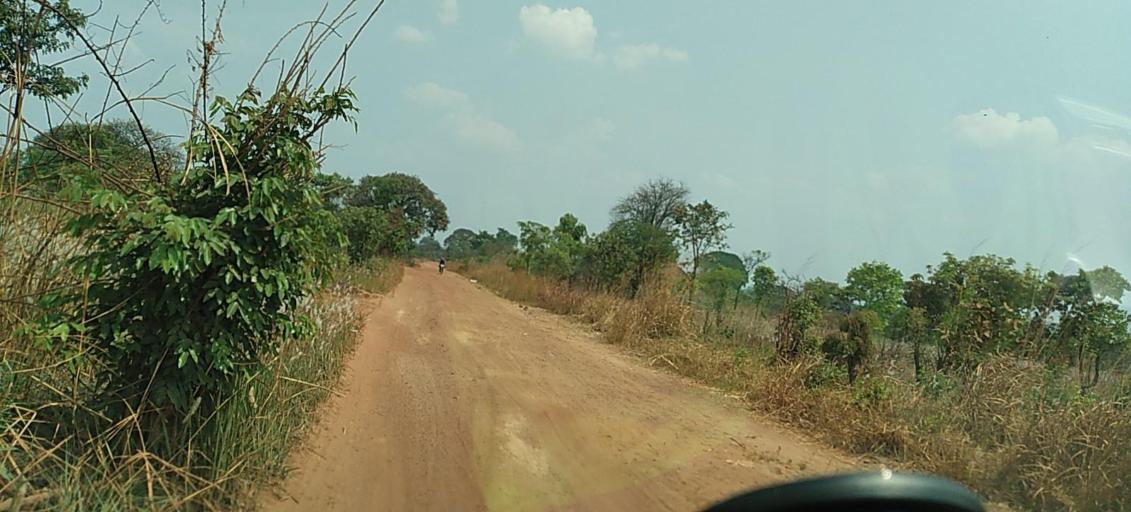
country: ZM
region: North-Western
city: Kansanshi
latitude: -12.1014
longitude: 26.3643
